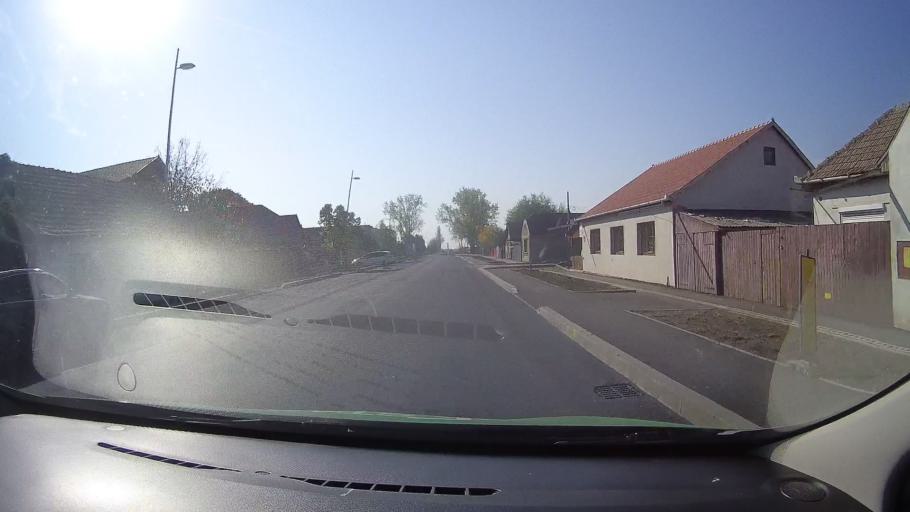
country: RO
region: Bihor
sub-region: Municipiul Salonta
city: Salonta
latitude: 46.7948
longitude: 21.6650
